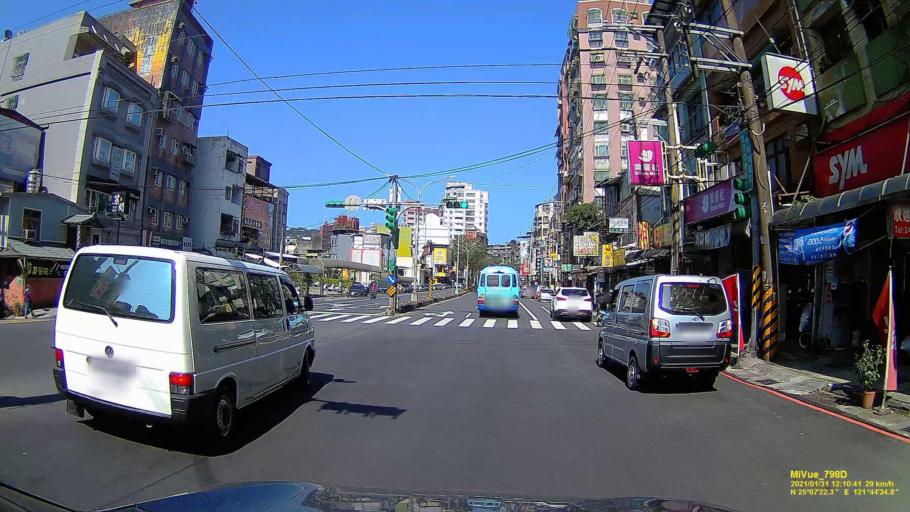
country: TW
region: Taiwan
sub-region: Keelung
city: Keelung
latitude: 25.1232
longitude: 121.7430
